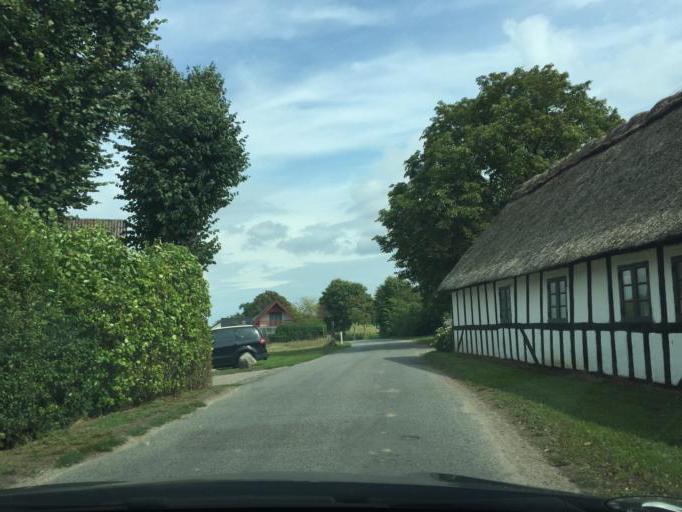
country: DK
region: South Denmark
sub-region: Assens Kommune
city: Vissenbjerg
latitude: 55.4045
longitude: 10.1873
